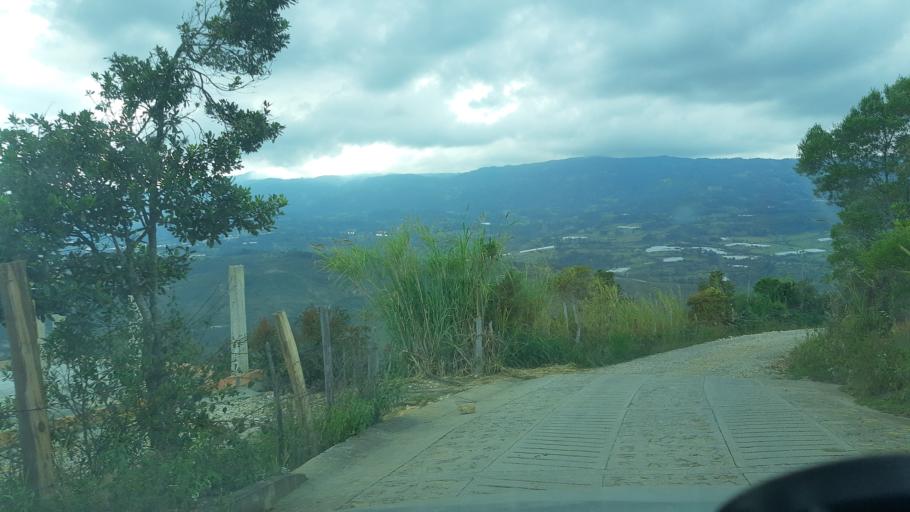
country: CO
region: Boyaca
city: Santa Sofia
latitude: 5.7448
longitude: -73.5665
